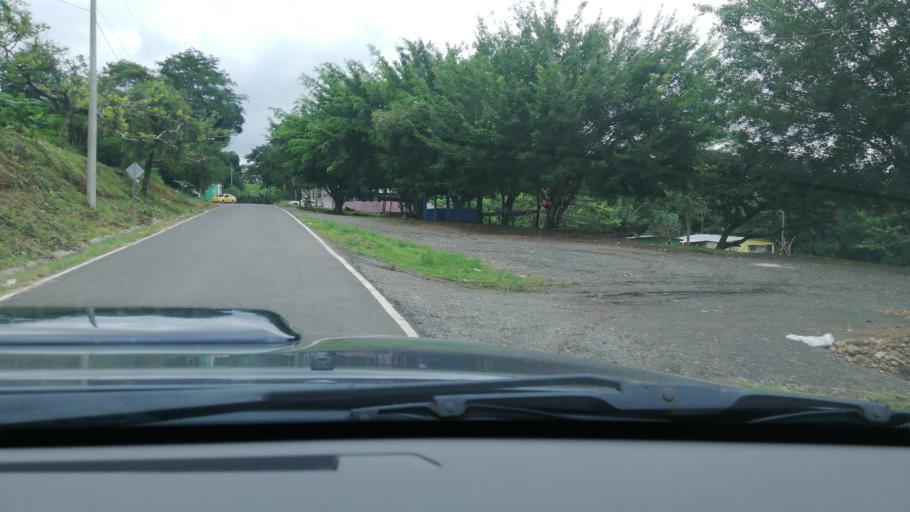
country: PA
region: Panama
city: Cerro Azul
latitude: 9.1122
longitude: -79.4438
